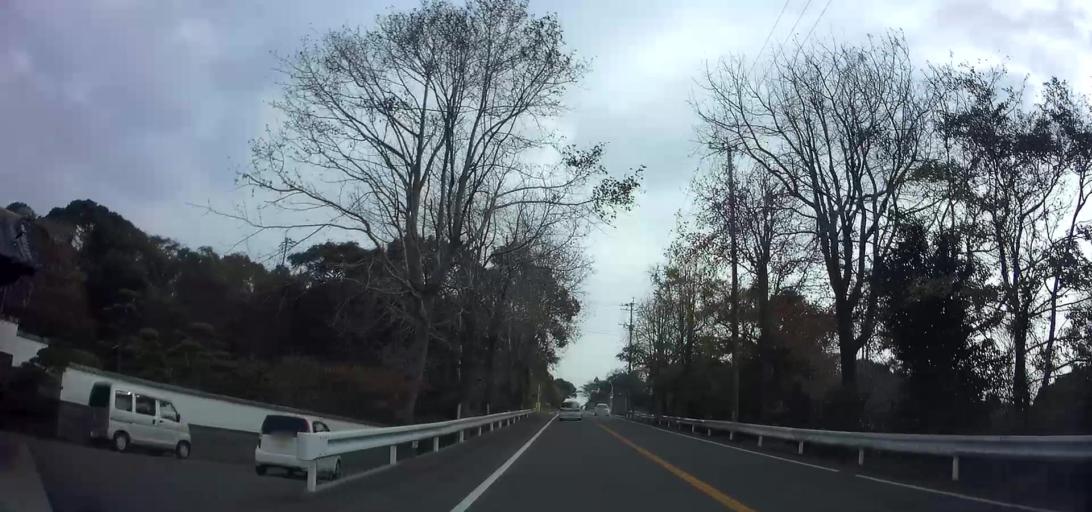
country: JP
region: Nagasaki
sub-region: Isahaya-shi
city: Isahaya
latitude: 32.7975
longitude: 130.1444
